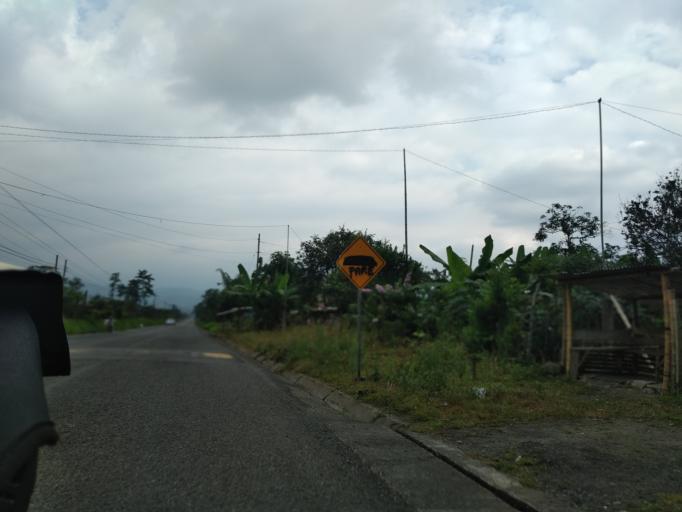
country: EC
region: Cotopaxi
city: La Mana
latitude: -0.8813
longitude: -79.1607
